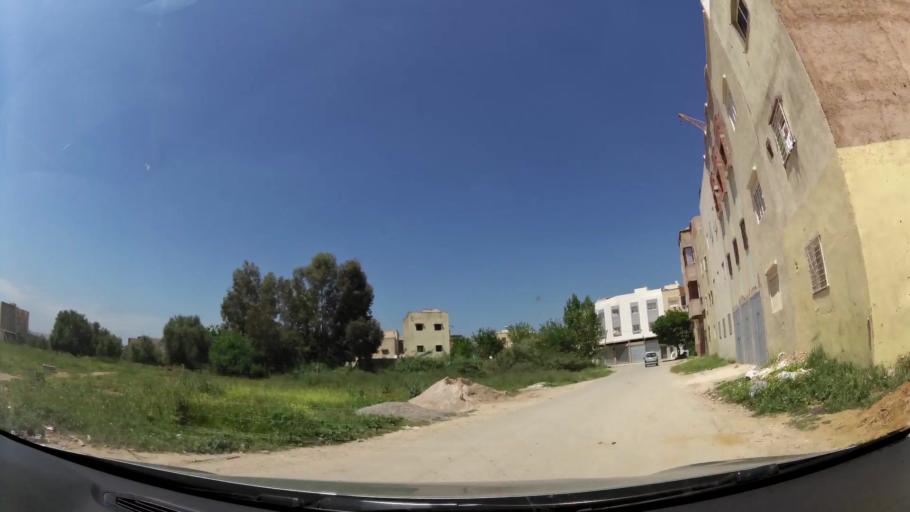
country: MA
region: Fes-Boulemane
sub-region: Fes
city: Fes
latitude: 34.0255
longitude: -5.0472
